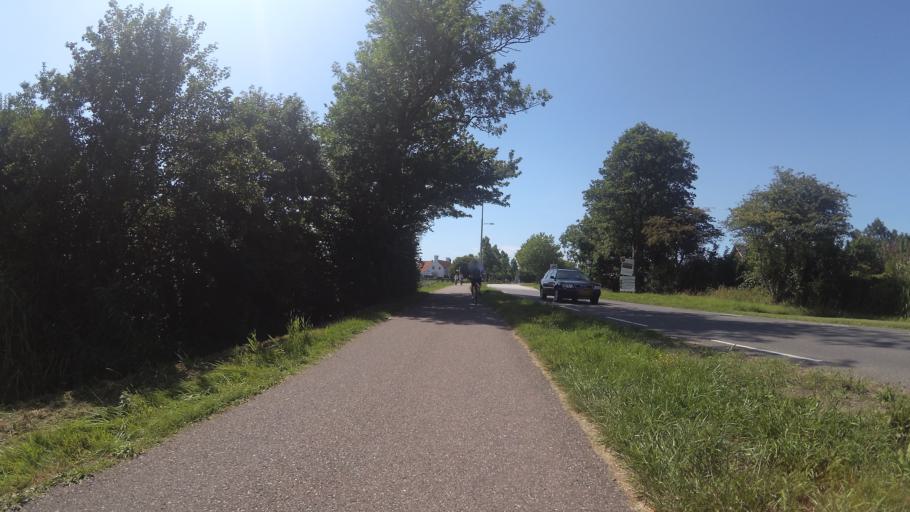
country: NL
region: Zeeland
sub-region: Gemeente Vlissingen
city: Vlissingen
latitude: 51.4825
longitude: 3.5641
